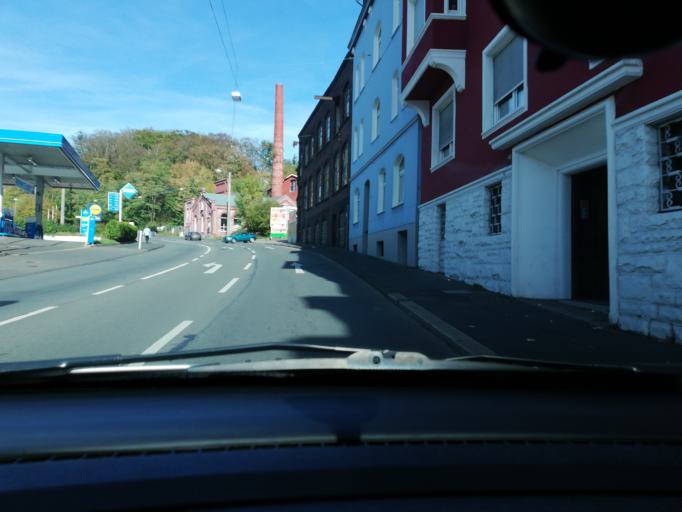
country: DE
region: North Rhine-Westphalia
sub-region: Regierungsbezirk Dusseldorf
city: Wuppertal
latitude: 51.2844
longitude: 7.2088
